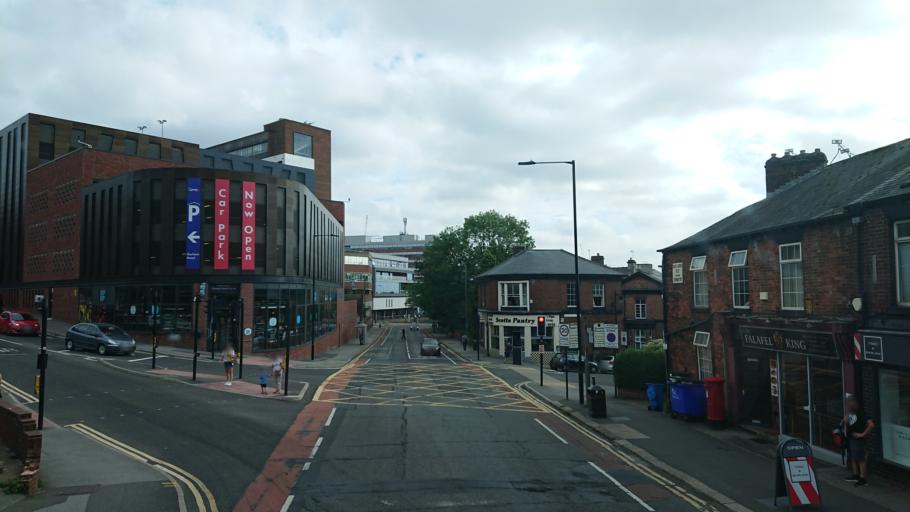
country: GB
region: England
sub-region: Sheffield
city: Sheffield
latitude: 53.3792
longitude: -1.4895
